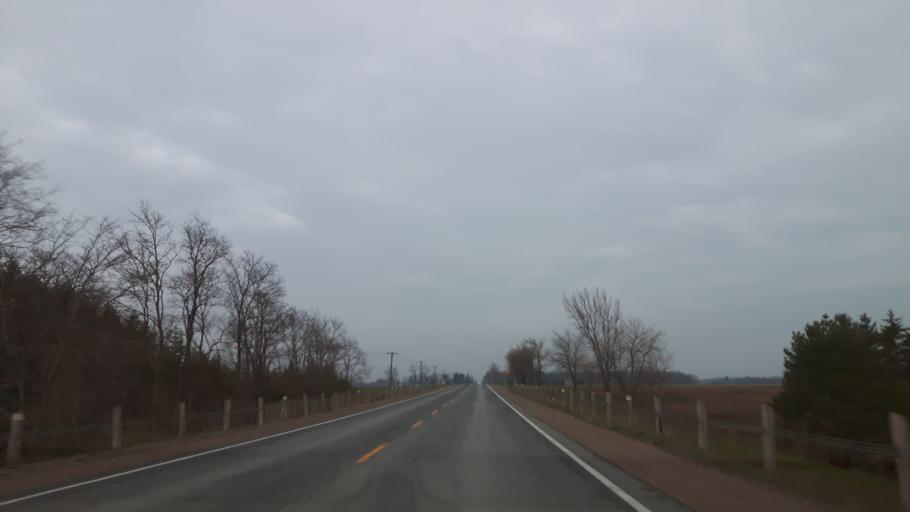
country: CA
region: Ontario
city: Bluewater
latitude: 43.5147
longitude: -81.6938
